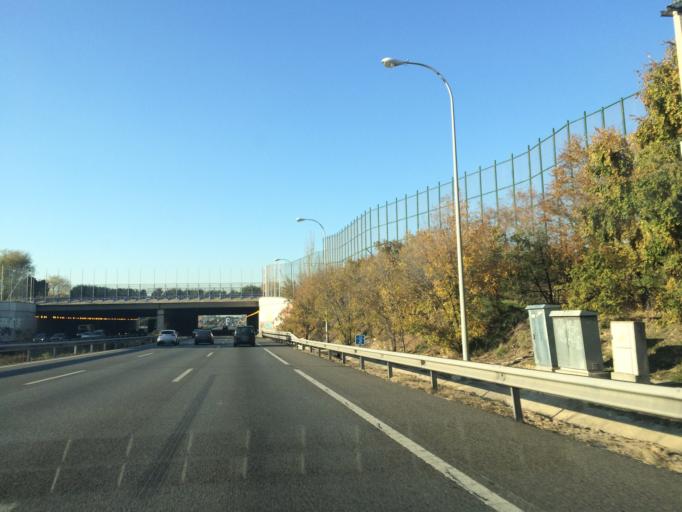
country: ES
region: Madrid
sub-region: Provincia de Madrid
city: Alcorcon
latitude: 40.3698
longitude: -3.7988
